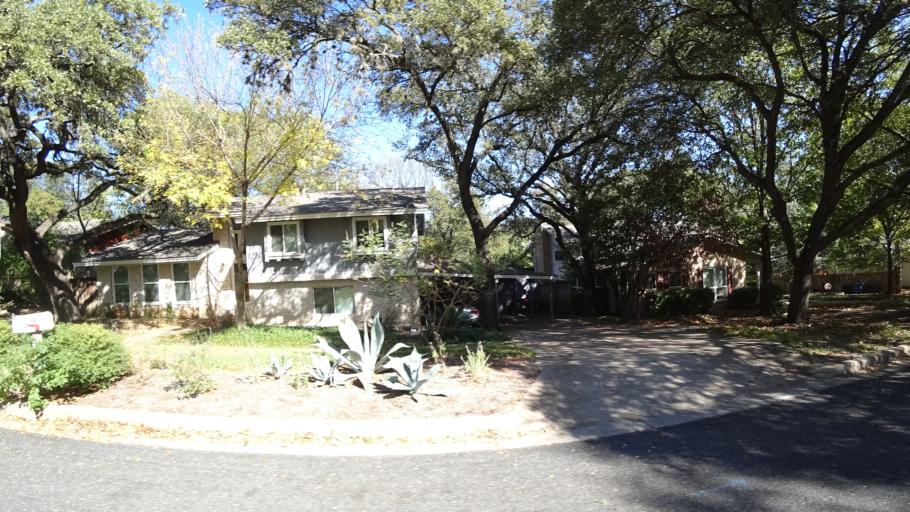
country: US
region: Texas
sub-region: Williamson County
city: Jollyville
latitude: 30.3801
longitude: -97.7474
